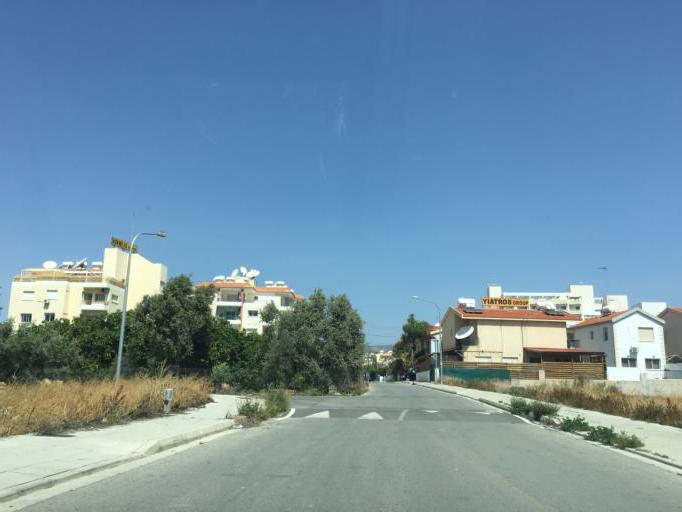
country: CY
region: Limassol
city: Mouttagiaka
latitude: 34.6976
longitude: 33.0870
